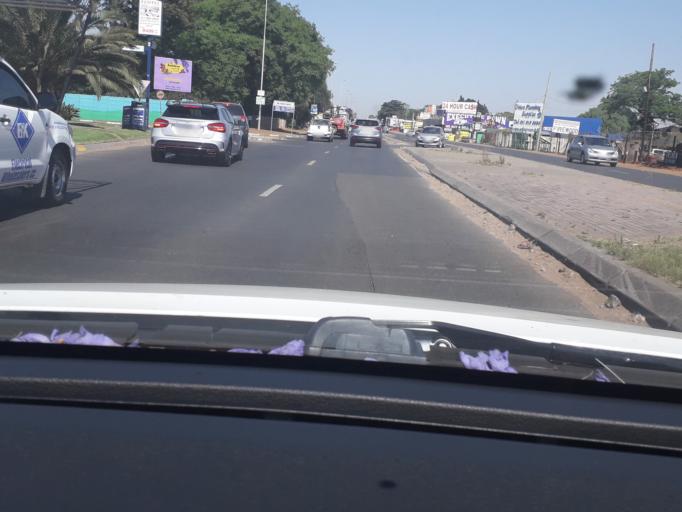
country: ZA
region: Gauteng
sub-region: Ekurhuleni Metropolitan Municipality
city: Boksburg
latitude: -26.1793
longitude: 28.2783
